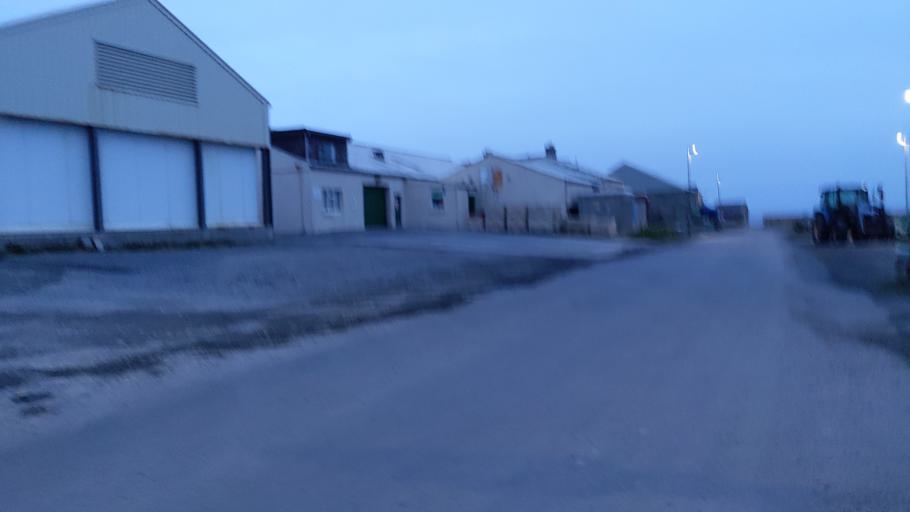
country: GB
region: Scotland
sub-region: Orkney Islands
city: Kirkwall
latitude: 59.3243
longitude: -2.9752
